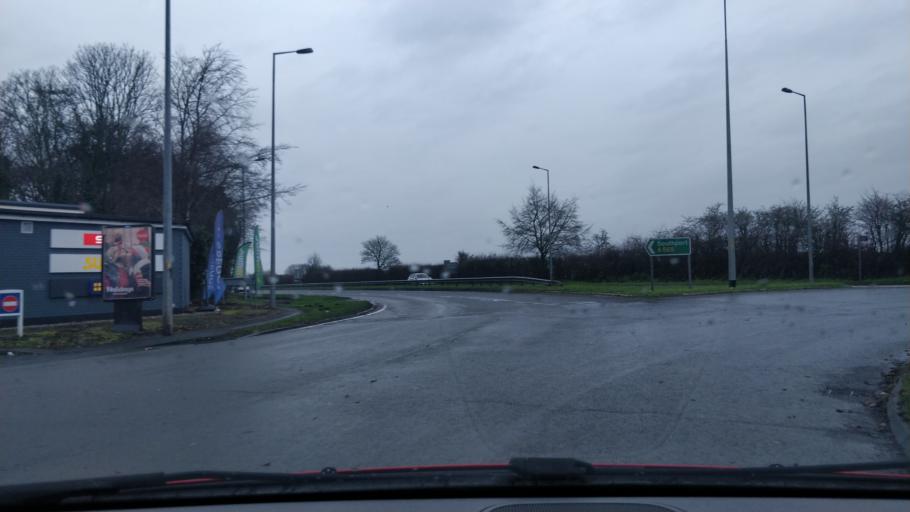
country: GB
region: England
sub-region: Sefton
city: Formby
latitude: 53.5686
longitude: -3.0480
